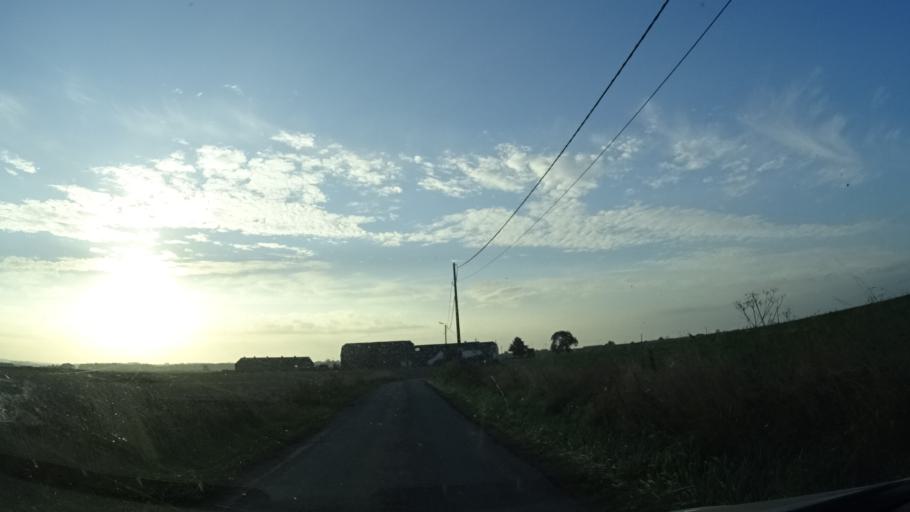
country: BE
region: Wallonia
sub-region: Province du Hainaut
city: Beaumont
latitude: 50.2474
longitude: 4.2625
